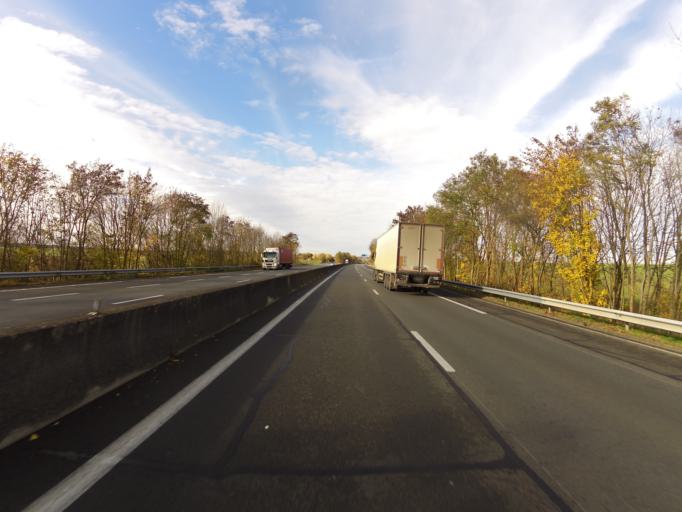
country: FR
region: Picardie
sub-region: Departement de l'Aisne
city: Couvron-et-Aumencourt
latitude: 49.6615
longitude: 3.5416
